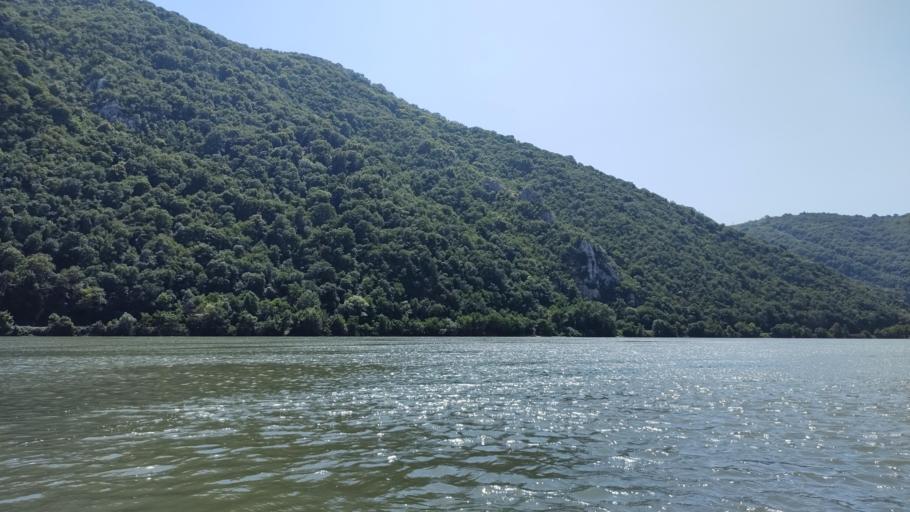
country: RO
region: Caras-Severin
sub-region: Comuna Pescari
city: Coronini
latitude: 44.6543
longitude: 21.7226
